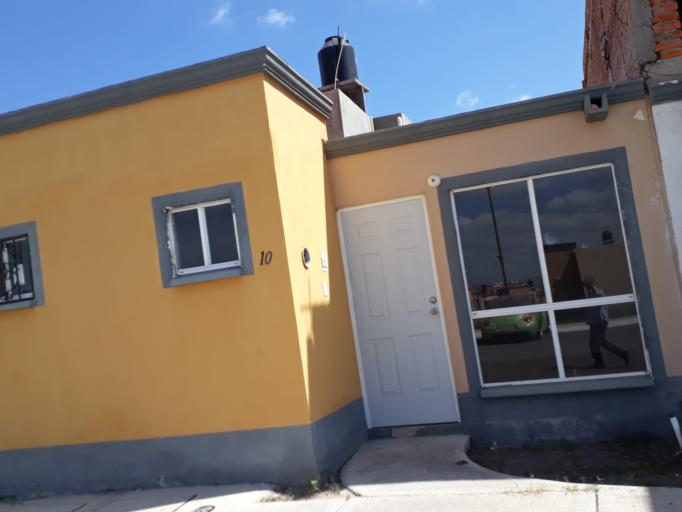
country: MX
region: Aguascalientes
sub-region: Aguascalientes
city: San Sebastian [Fraccionamiento]
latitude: 21.7940
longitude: -102.2739
